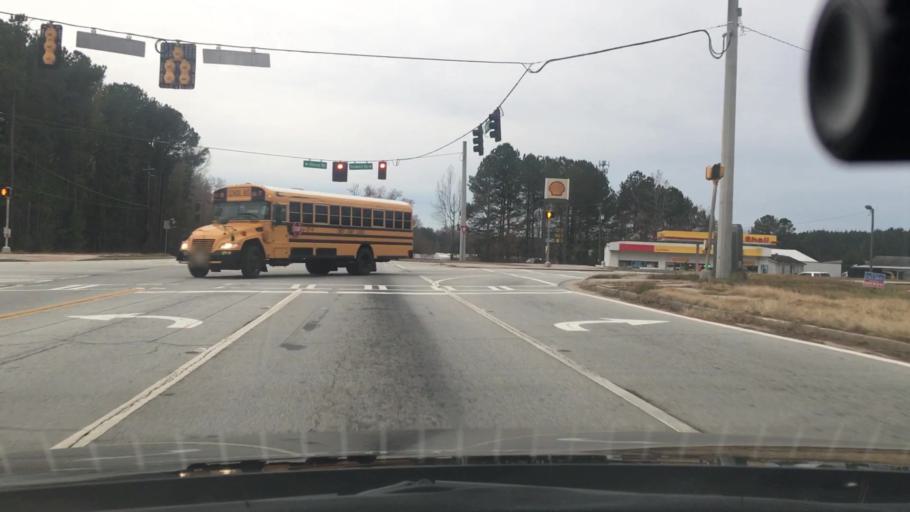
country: US
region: Georgia
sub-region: Fayette County
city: Peachtree City
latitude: 33.3610
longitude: -84.6338
